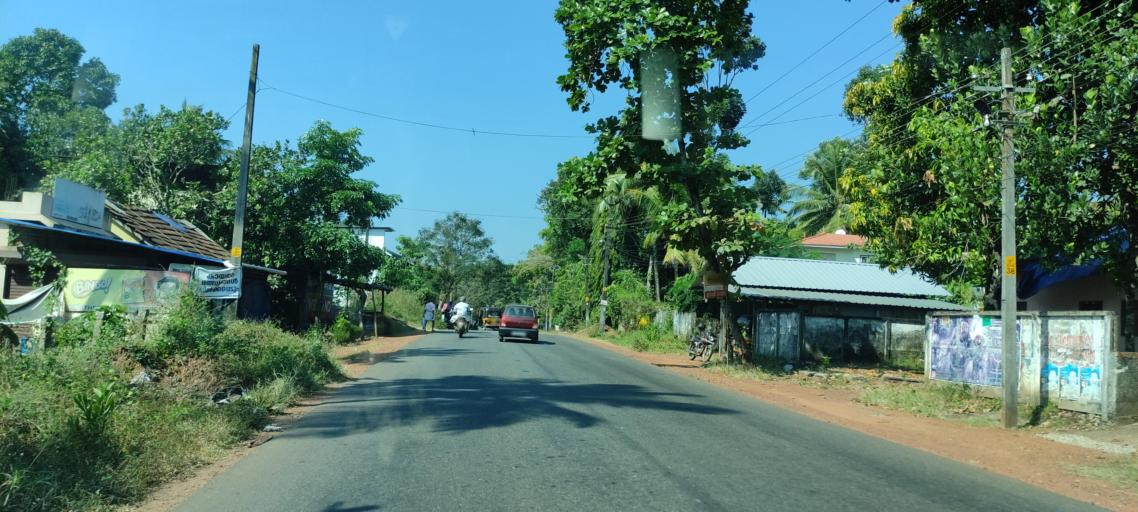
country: IN
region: Kerala
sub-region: Kollam
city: Panmana
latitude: 9.0431
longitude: 76.6189
